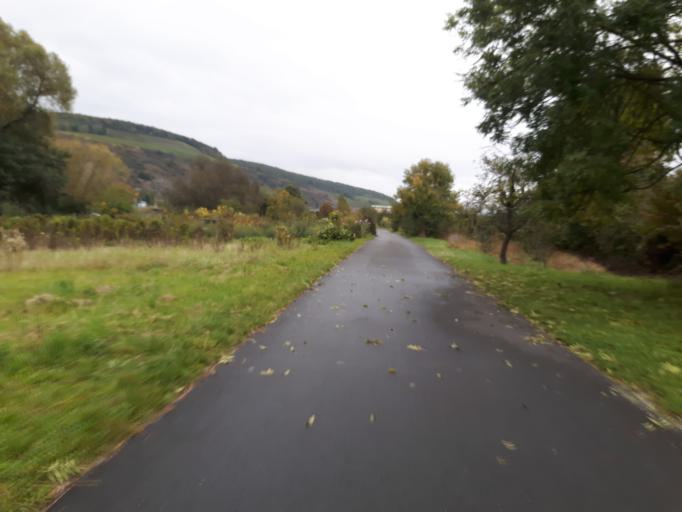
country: DE
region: Bavaria
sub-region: Regierungsbezirk Unterfranken
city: Erlabrunn
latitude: 49.8585
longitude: 9.8477
